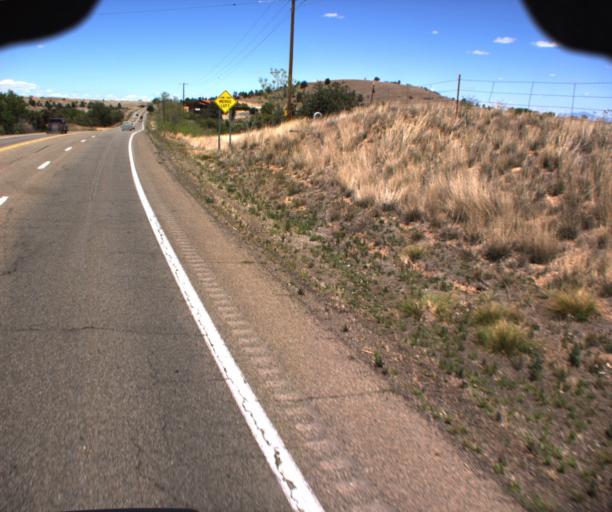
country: US
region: Arizona
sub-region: Yavapai County
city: Prescott
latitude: 34.6189
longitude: -112.4241
